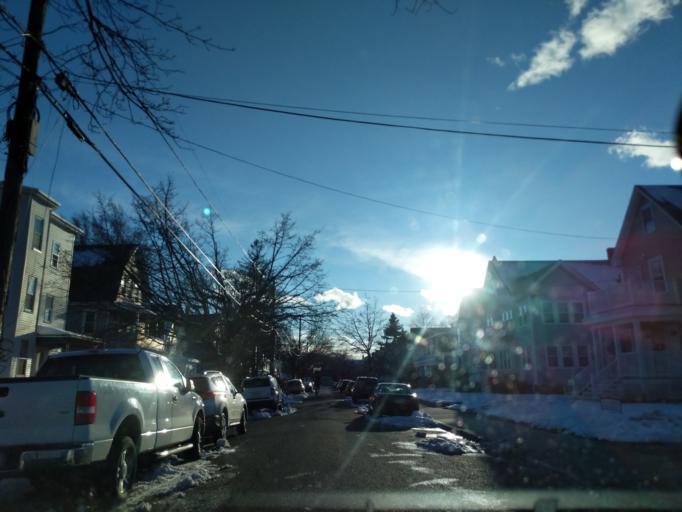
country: US
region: Massachusetts
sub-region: Middlesex County
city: Medford
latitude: 42.4035
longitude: -71.1097
